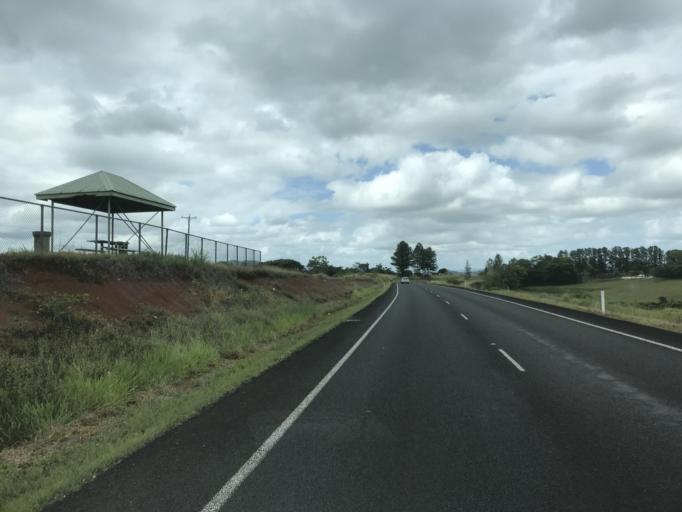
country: AU
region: Queensland
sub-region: Cassowary Coast
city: Innisfail
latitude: -17.5783
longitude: 145.9701
